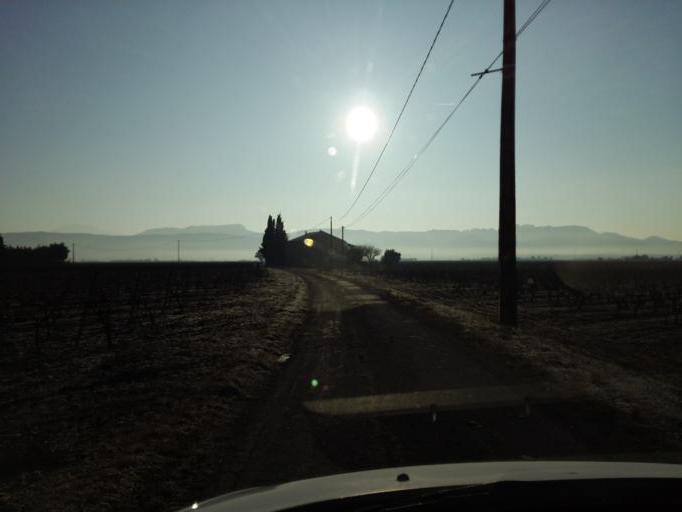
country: FR
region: Provence-Alpes-Cote d'Azur
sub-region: Departement du Vaucluse
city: Sablet
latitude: 44.2102
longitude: 4.9664
